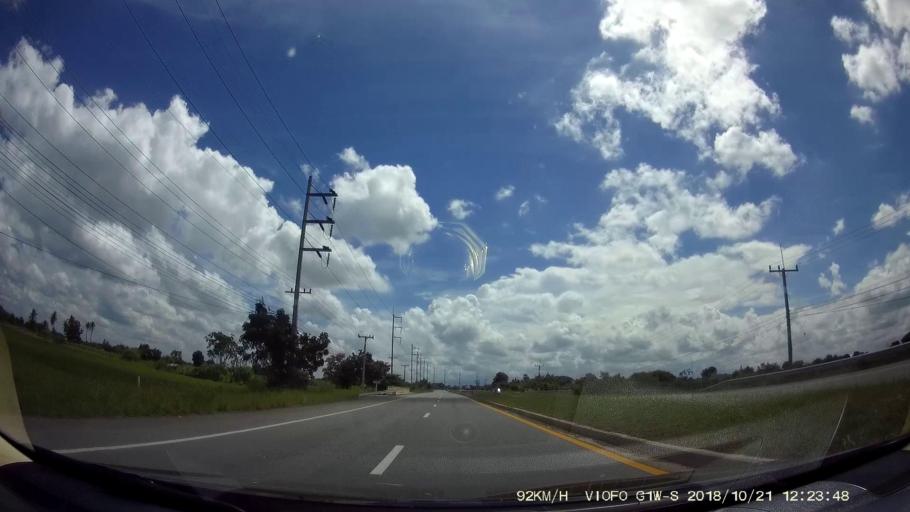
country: TH
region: Nakhon Ratchasima
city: Dan Khun Thot
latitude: 15.2407
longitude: 101.7863
